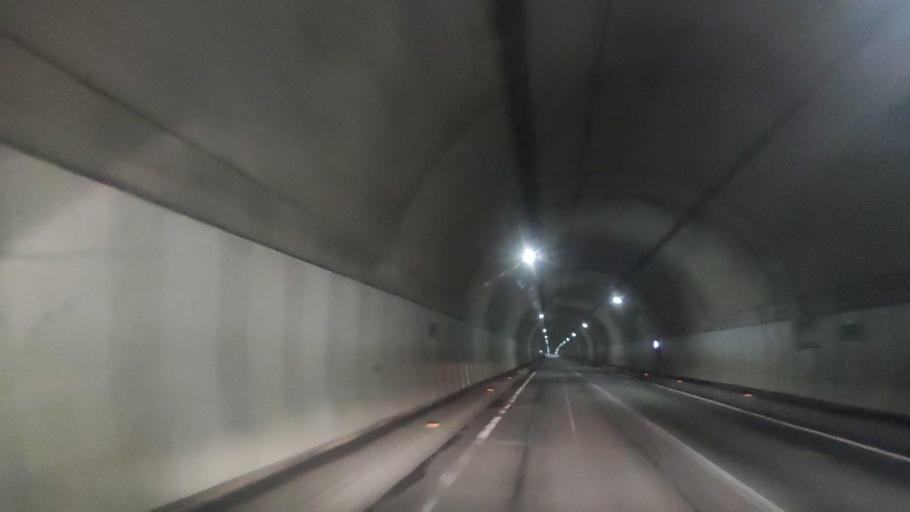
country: JP
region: Hokkaido
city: Date
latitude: 42.5531
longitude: 141.0768
